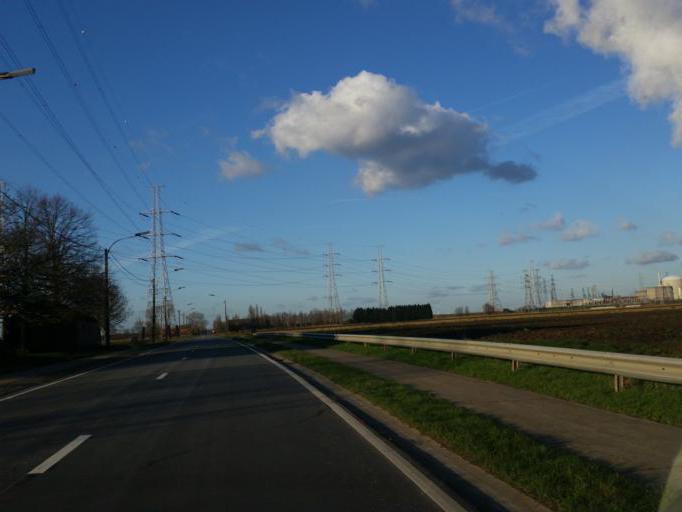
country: BE
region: Flanders
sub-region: Provincie Oost-Vlaanderen
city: Beveren
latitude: 51.3101
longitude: 4.2517
